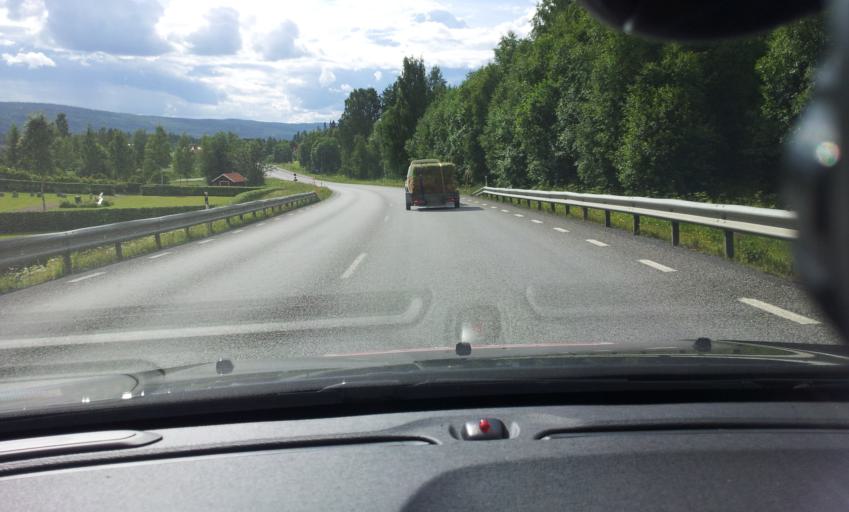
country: SE
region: Jaemtland
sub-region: Are Kommun
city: Jarpen
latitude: 63.3112
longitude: 13.6537
